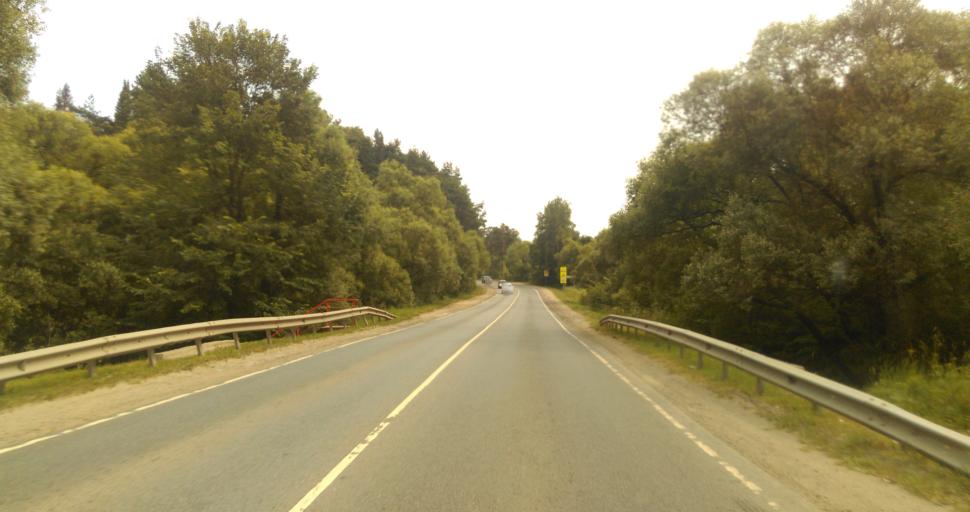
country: RU
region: Moskovskaya
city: Zhitnevo
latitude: 55.3689
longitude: 37.8957
